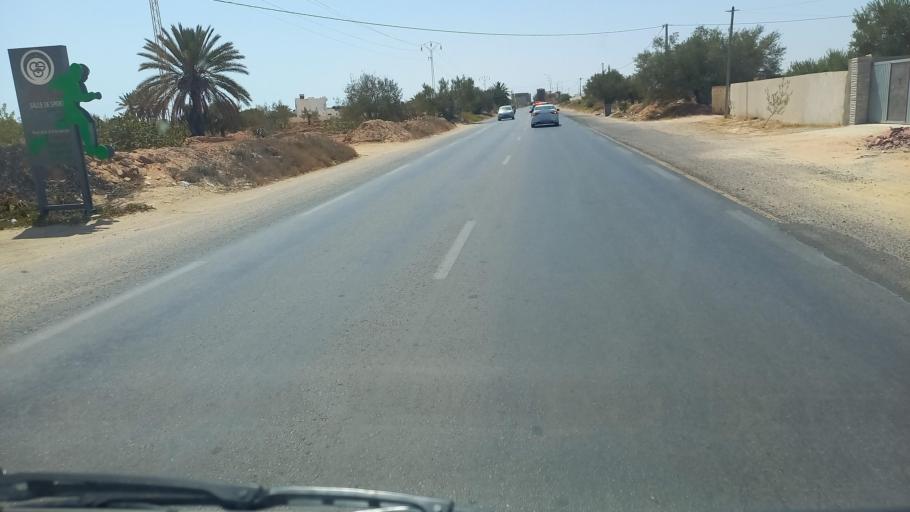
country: TN
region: Madanin
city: Houmt Souk
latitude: 33.7902
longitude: 10.8879
